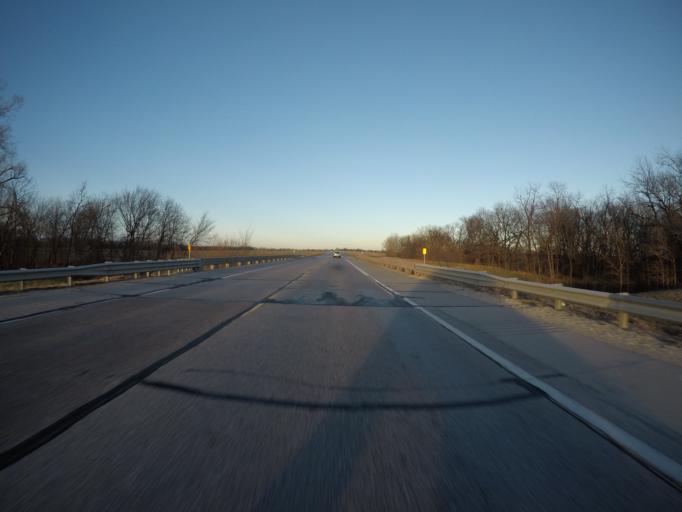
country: US
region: Kansas
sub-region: Marion County
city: Peabody
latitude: 38.1705
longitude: -97.1952
